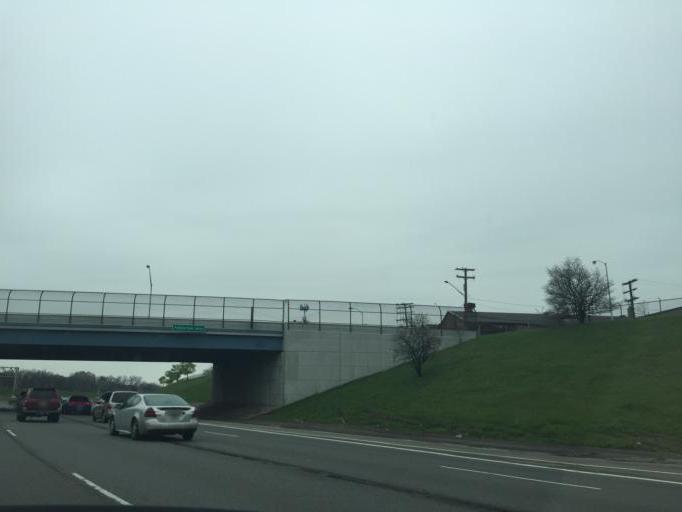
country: US
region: Michigan
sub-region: Wayne County
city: Highland Park
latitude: 42.3819
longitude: -83.1477
